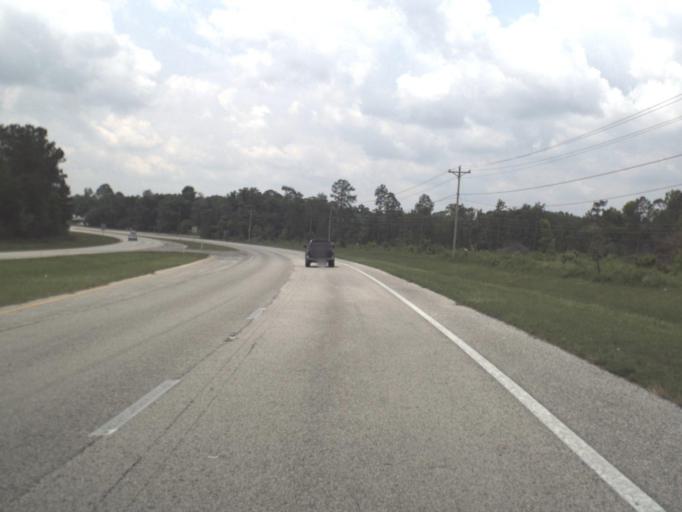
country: US
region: Florida
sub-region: Clay County
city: Green Cove Springs
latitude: 29.9380
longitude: -81.6877
